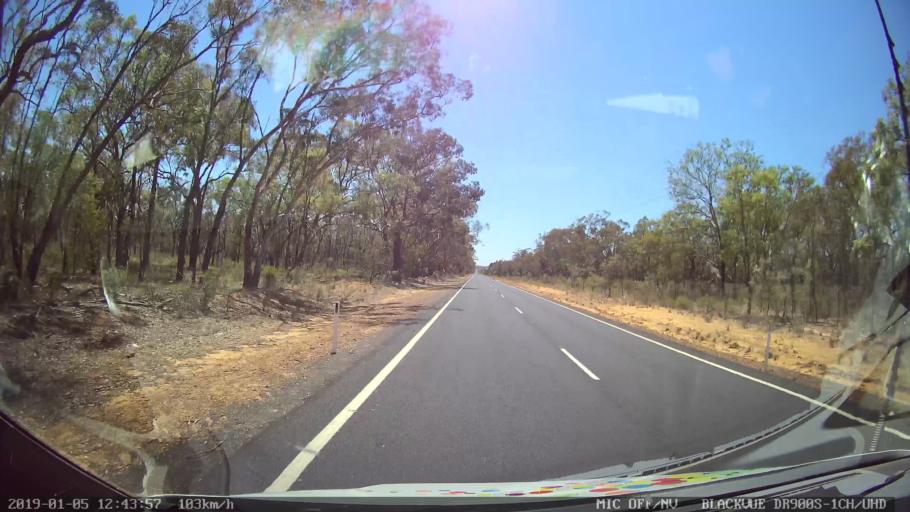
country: AU
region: New South Wales
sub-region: Warrumbungle Shire
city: Coonabarabran
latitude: -31.1427
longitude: 149.5309
